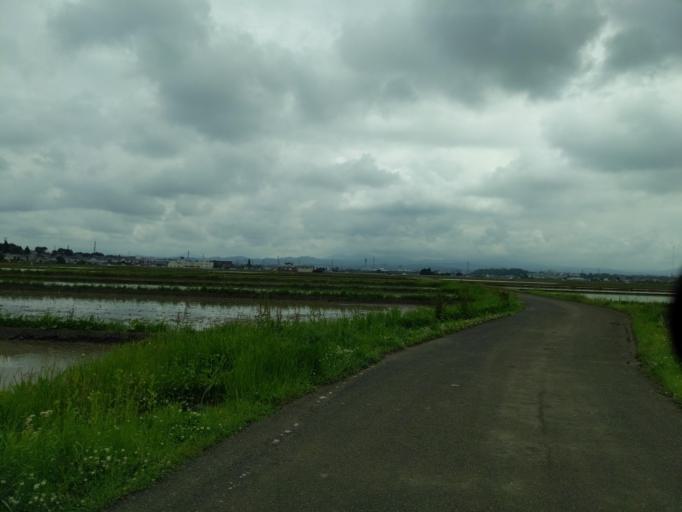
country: JP
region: Fukushima
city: Koriyama
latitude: 37.3709
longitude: 140.3339
